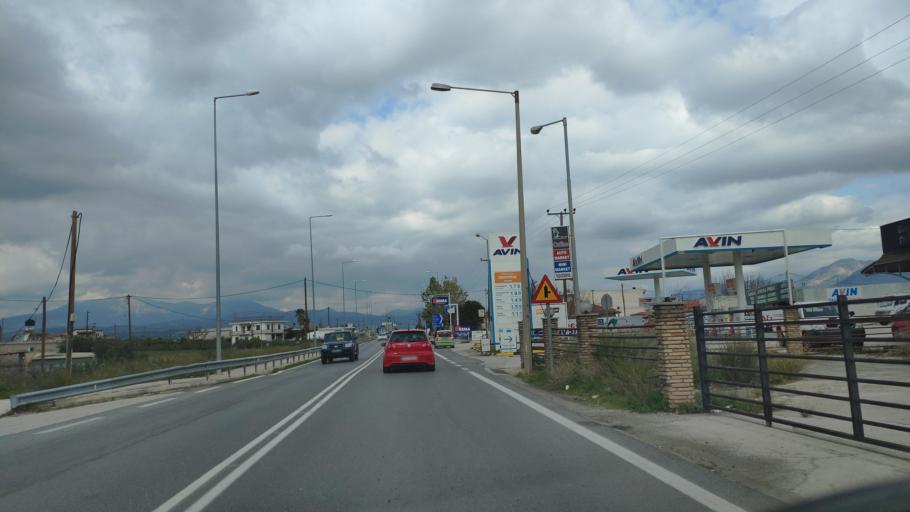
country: GR
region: Peloponnese
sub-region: Nomos Argolidos
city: Argos
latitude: 37.6481
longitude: 22.7295
